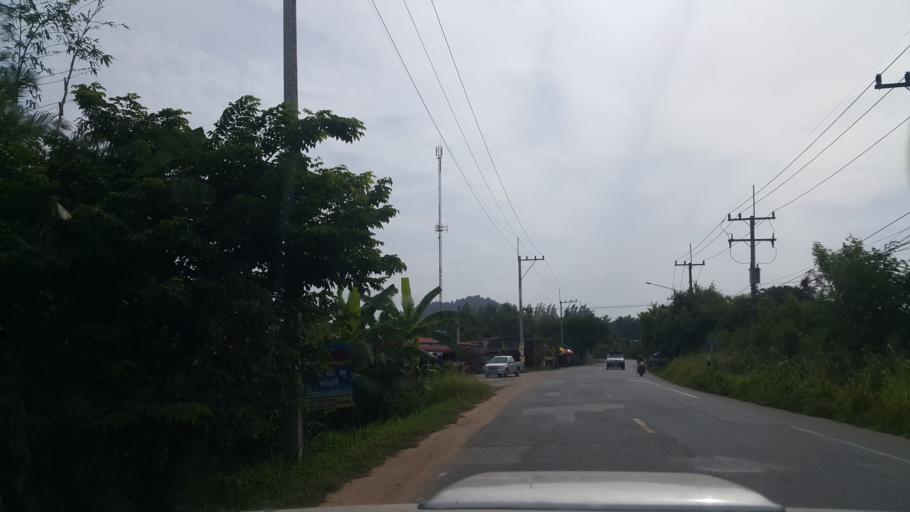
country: TH
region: Rayong
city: Ban Chang
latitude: 12.7677
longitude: 101.0114
